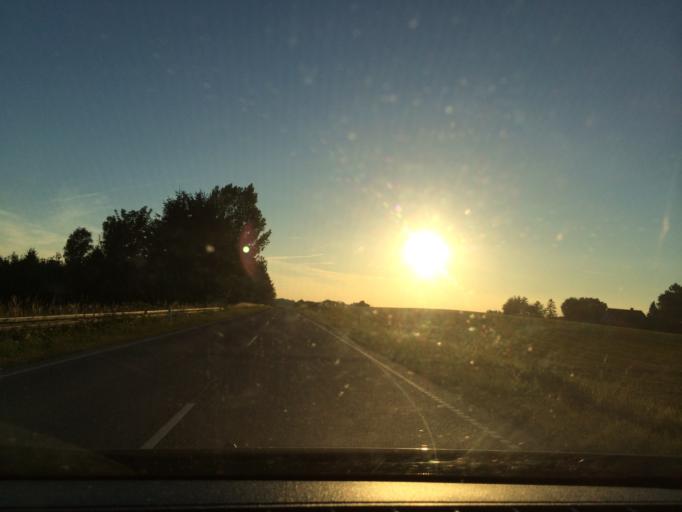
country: DK
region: Zealand
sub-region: Vordingborg Kommune
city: Praesto
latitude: 55.0094
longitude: 12.1341
